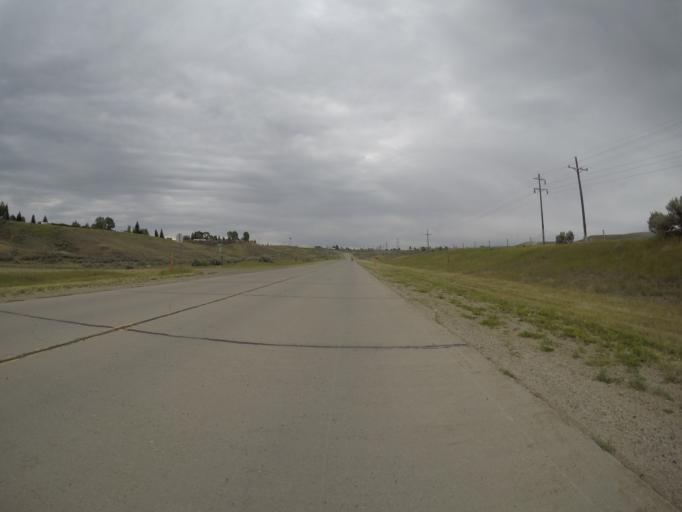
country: US
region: Wyoming
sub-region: Lincoln County
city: Kemmerer
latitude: 41.7986
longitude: -110.5477
